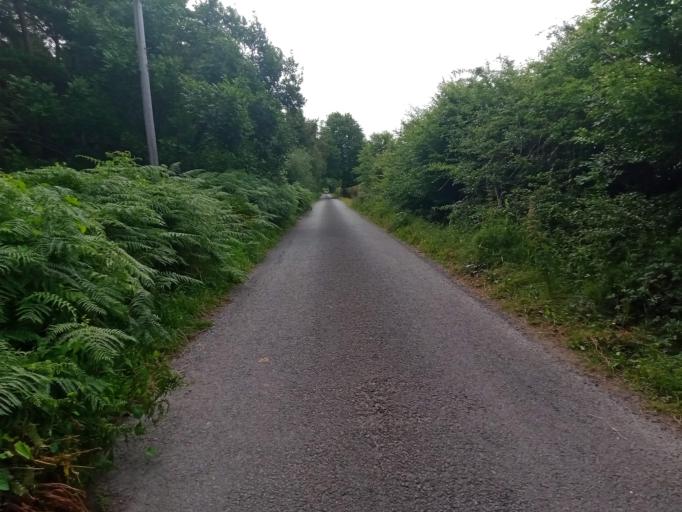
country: IE
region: Leinster
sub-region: Laois
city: Abbeyleix
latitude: 52.8822
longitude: -7.3559
